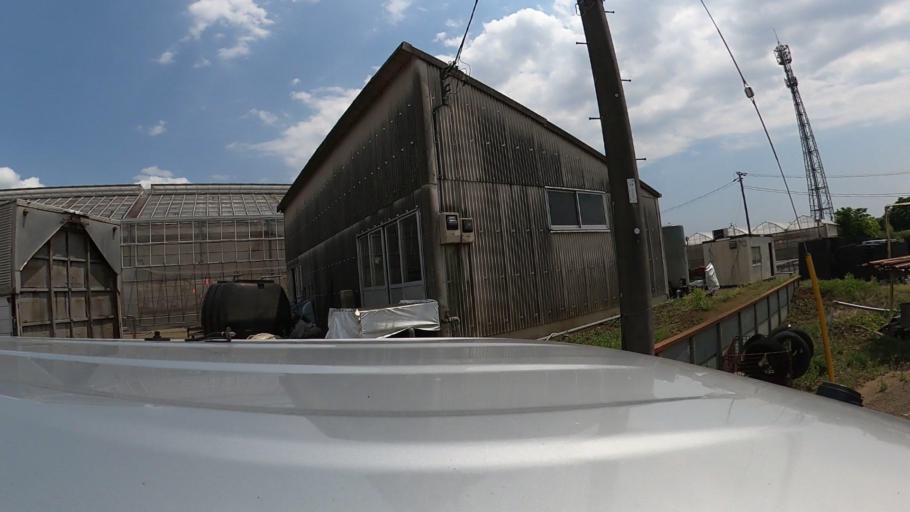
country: JP
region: Kanagawa
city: Chigasaki
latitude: 35.3898
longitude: 139.4217
